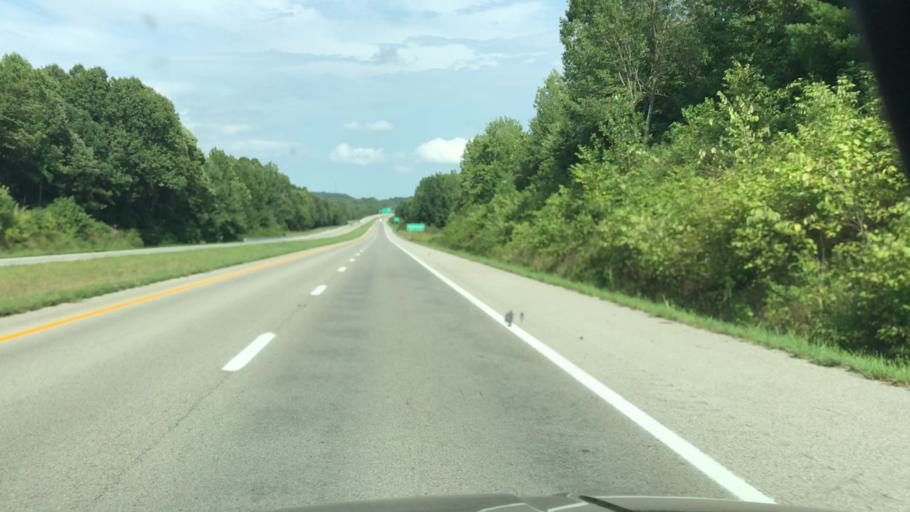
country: US
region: Kentucky
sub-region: Hopkins County
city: Nortonville
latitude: 37.2101
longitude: -87.4834
